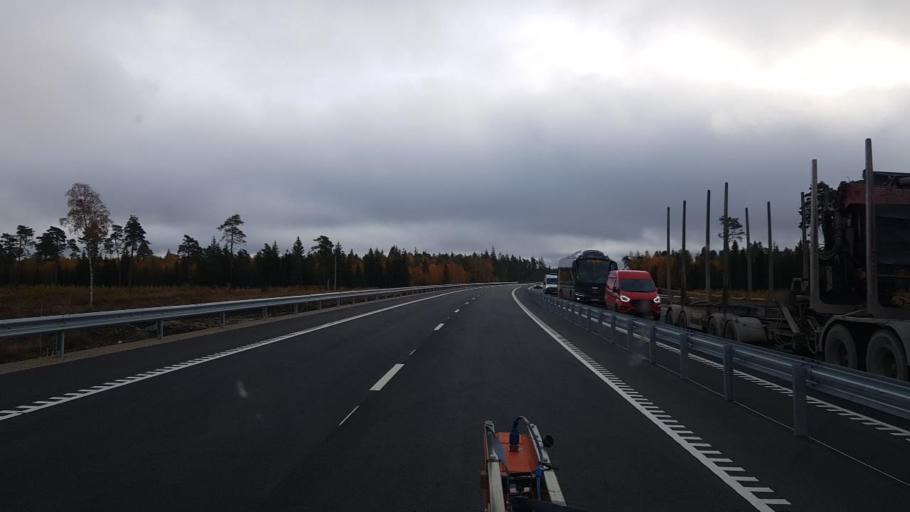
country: EE
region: Jaervamaa
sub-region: Paide linn
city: Paide
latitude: 59.0306
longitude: 25.5289
